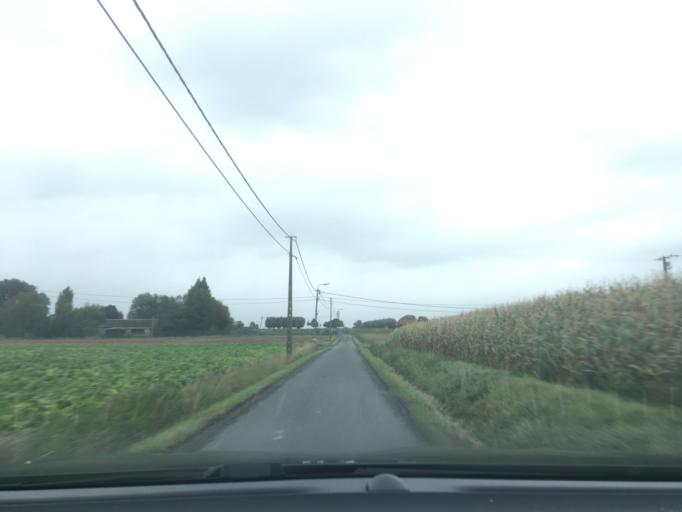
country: BE
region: Flanders
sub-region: Provincie West-Vlaanderen
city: Ledegem
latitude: 50.8858
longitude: 3.1324
